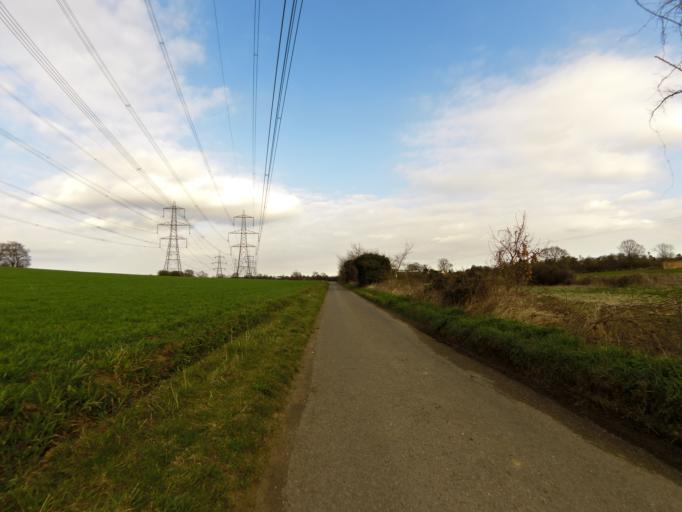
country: GB
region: England
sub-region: Suffolk
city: Ipswich
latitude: 52.0919
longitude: 1.1371
